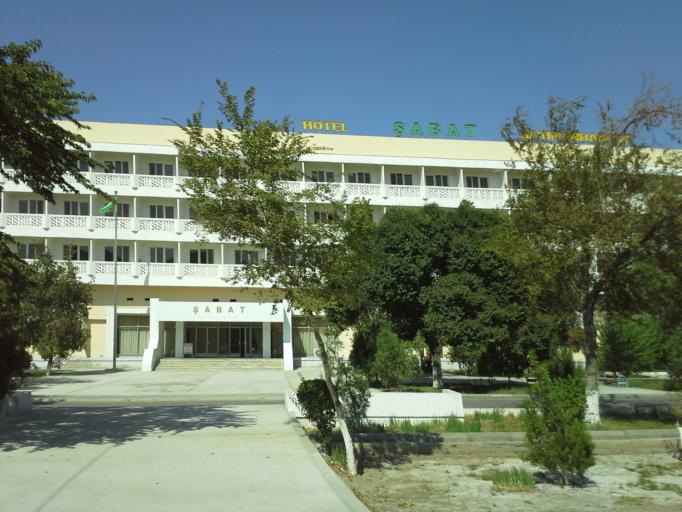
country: TM
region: Dasoguz
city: Dasoguz
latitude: 41.8339
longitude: 59.9680
